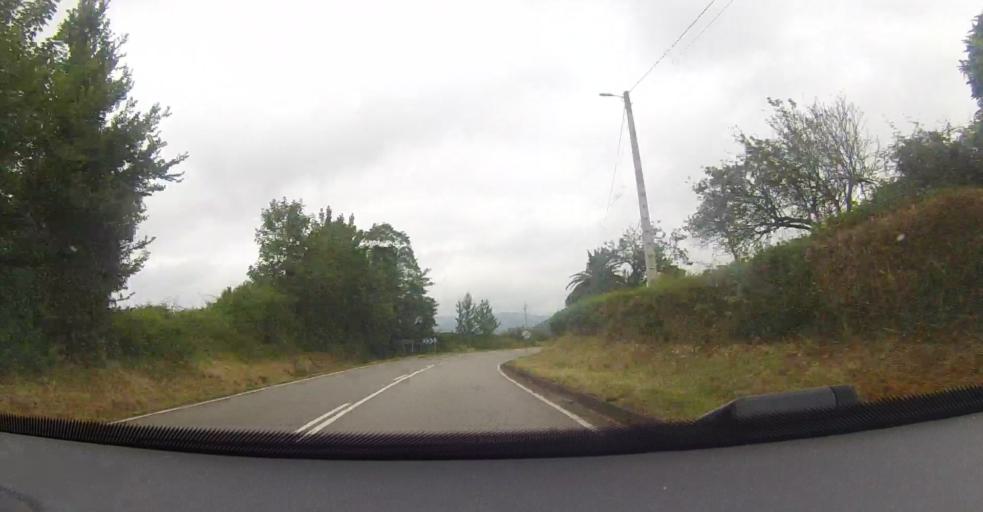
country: ES
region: Asturias
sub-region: Province of Asturias
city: Villaviciosa
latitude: 43.4950
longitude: -5.4290
